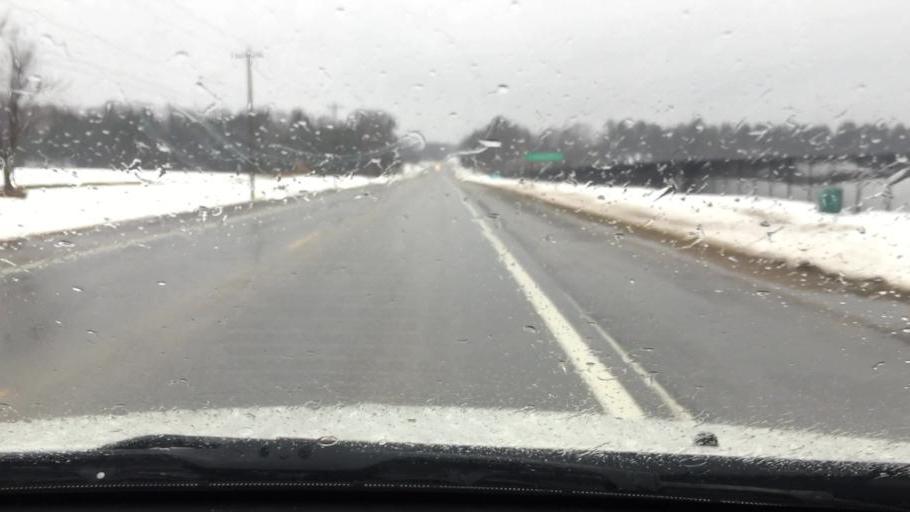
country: US
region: Michigan
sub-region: Charlevoix County
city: Charlevoix
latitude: 45.2784
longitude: -85.2285
